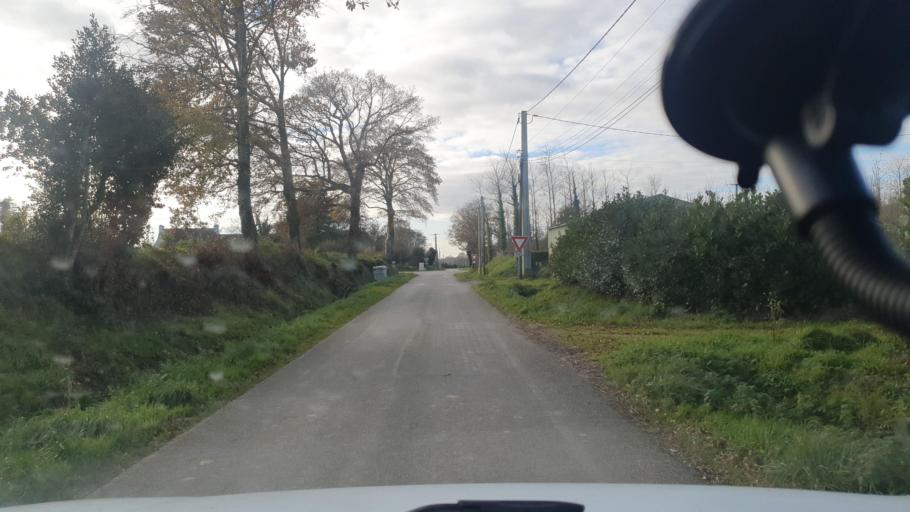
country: FR
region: Brittany
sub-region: Departement du Finistere
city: Briec
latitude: 48.1169
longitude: -4.0131
